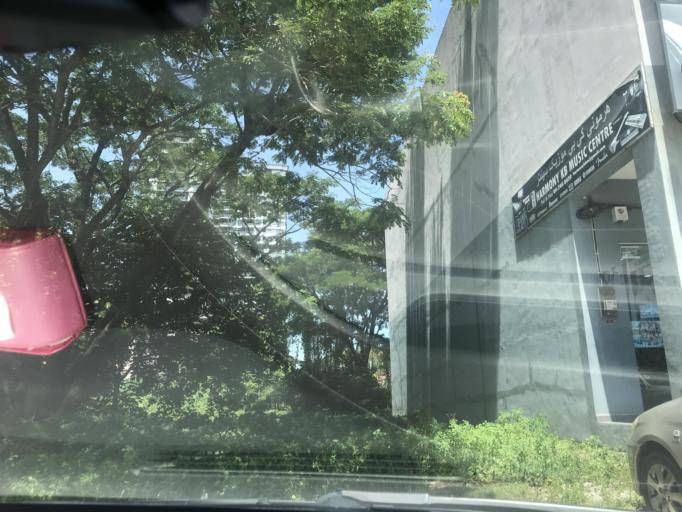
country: MY
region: Kelantan
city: Kota Bharu
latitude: 6.1317
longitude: 102.2474
